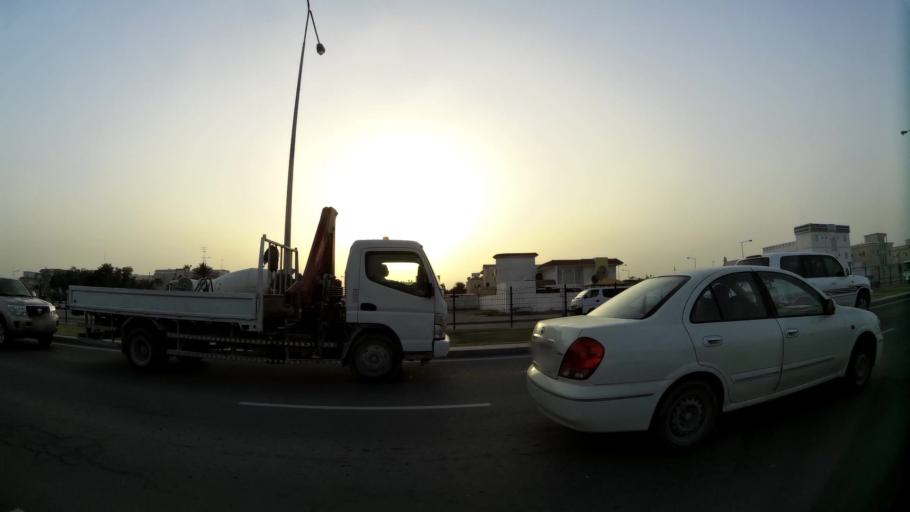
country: QA
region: Baladiyat ar Rayyan
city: Ar Rayyan
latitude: 25.2485
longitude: 51.4313
